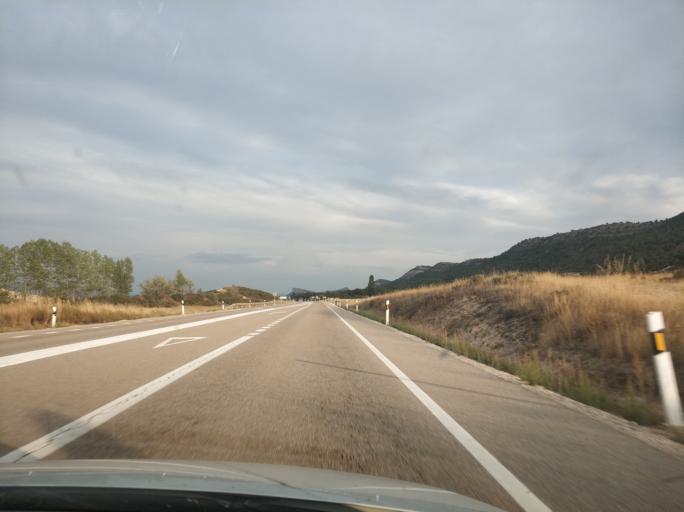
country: ES
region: Castille and Leon
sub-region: Provincia de Burgos
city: Mambrillas de Lara
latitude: 42.0987
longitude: -3.4935
